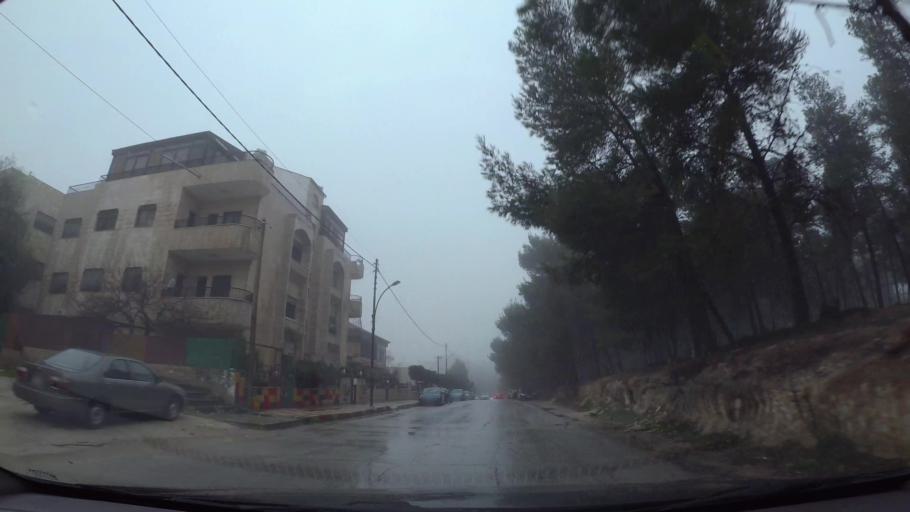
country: JO
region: Amman
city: Al Jubayhah
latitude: 32.0208
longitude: 35.8783
